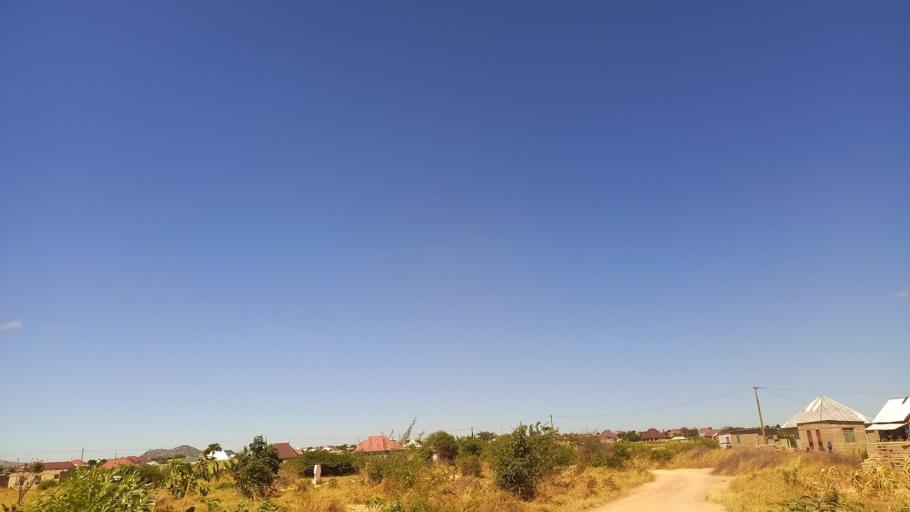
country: TZ
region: Dodoma
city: Dodoma
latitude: -6.1241
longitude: 35.6973
